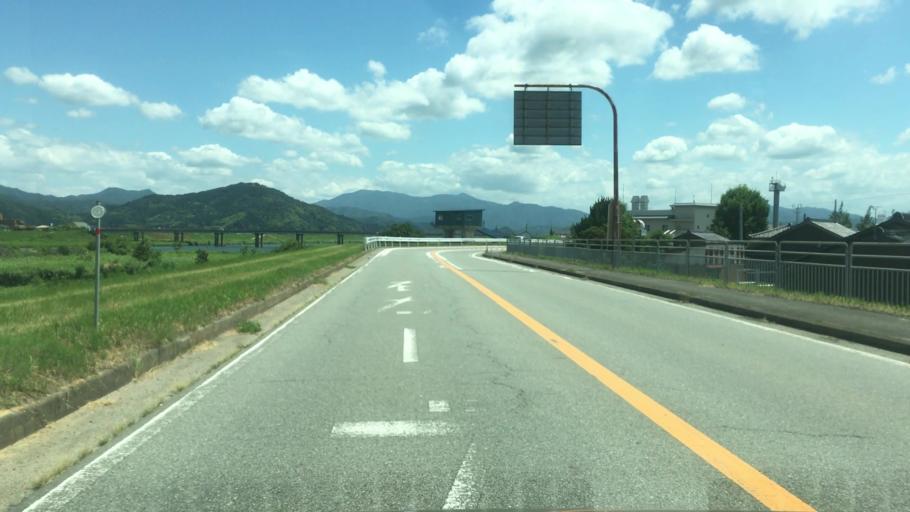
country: JP
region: Hyogo
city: Toyooka
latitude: 35.5485
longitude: 134.8258
